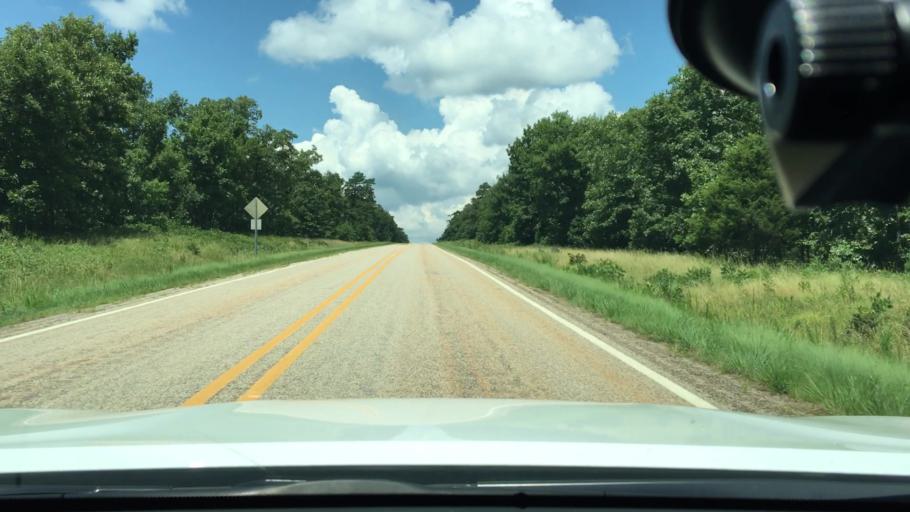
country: US
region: Arkansas
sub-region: Logan County
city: Paris
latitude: 35.1757
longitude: -93.5946
